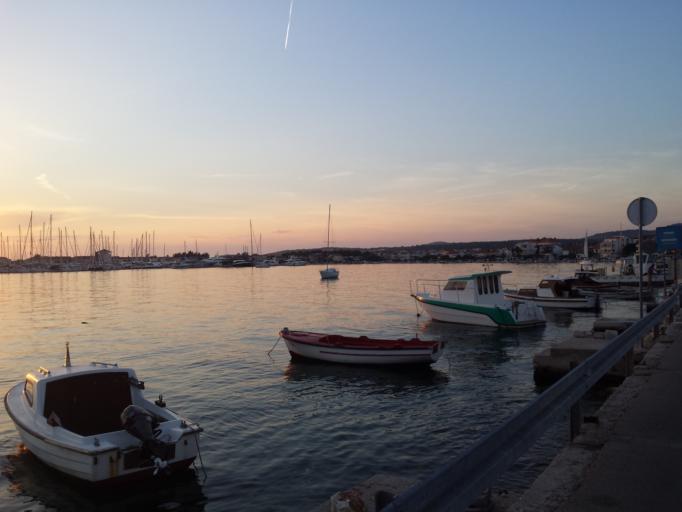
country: HR
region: Sibensko-Kniniska
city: Rogoznica
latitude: 43.5297
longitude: 15.9682
